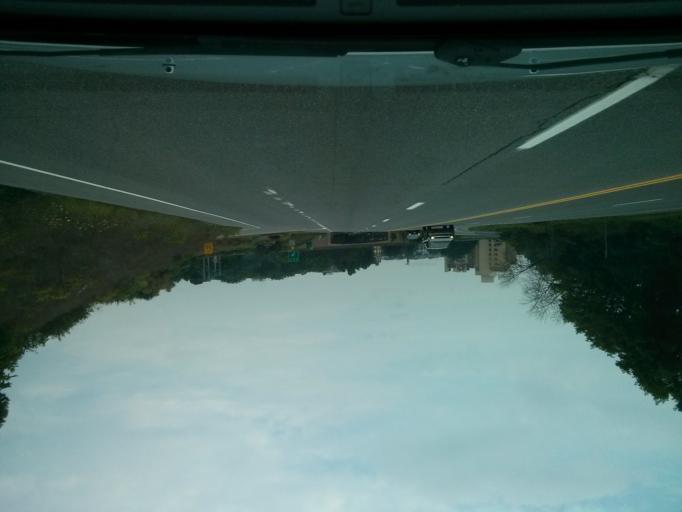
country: US
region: Pennsylvania
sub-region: Centre County
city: State College
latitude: 40.8032
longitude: -77.8485
